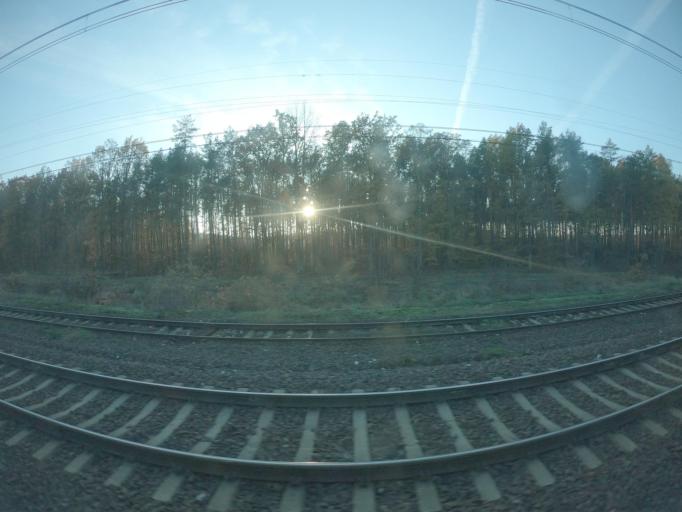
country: PL
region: Lubusz
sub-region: Powiat slubicki
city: Rzepin
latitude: 52.3040
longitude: 14.8705
